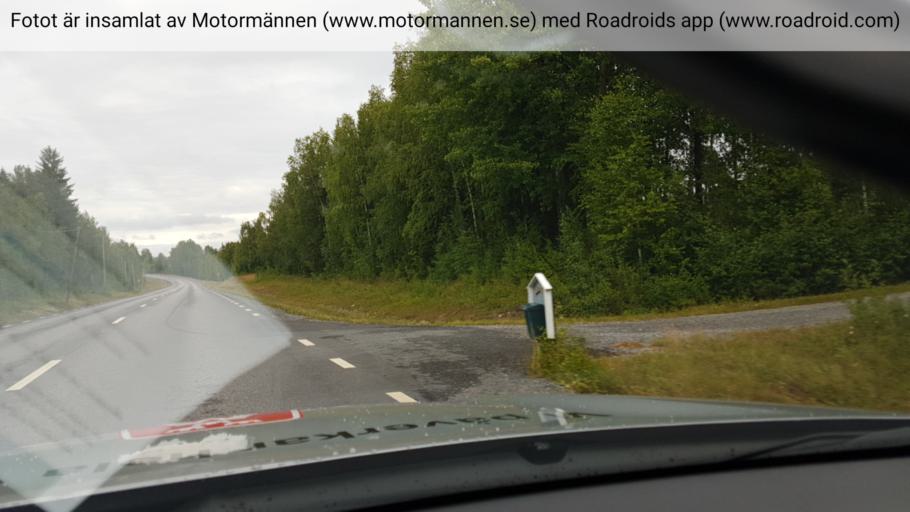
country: SE
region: Norrbotten
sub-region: Alvsbyns Kommun
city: AElvsbyn
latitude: 66.2775
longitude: 20.8236
